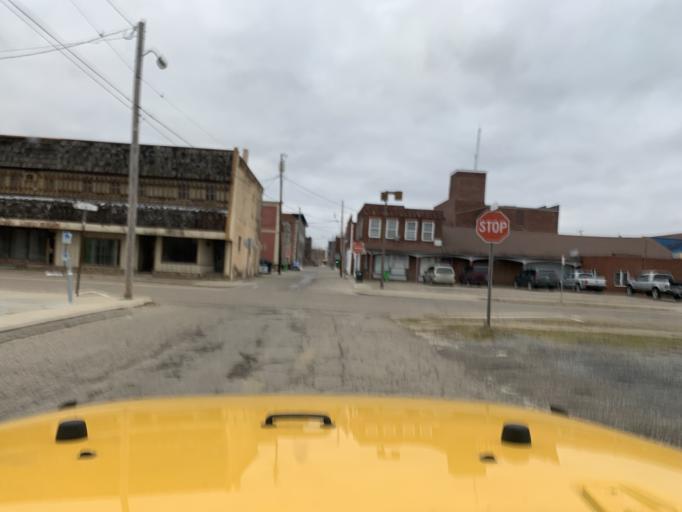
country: US
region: Ohio
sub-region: Tuscarawas County
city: Dover
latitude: 40.5195
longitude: -81.4775
